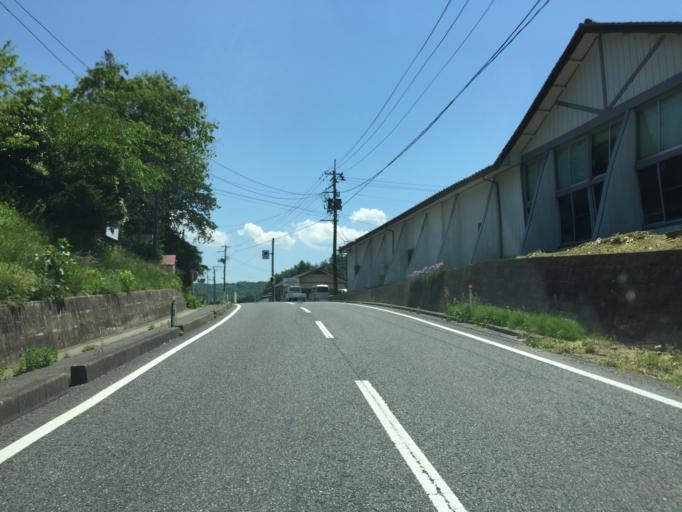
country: JP
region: Fukushima
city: Funehikimachi-funehiki
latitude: 37.4883
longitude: 140.5355
